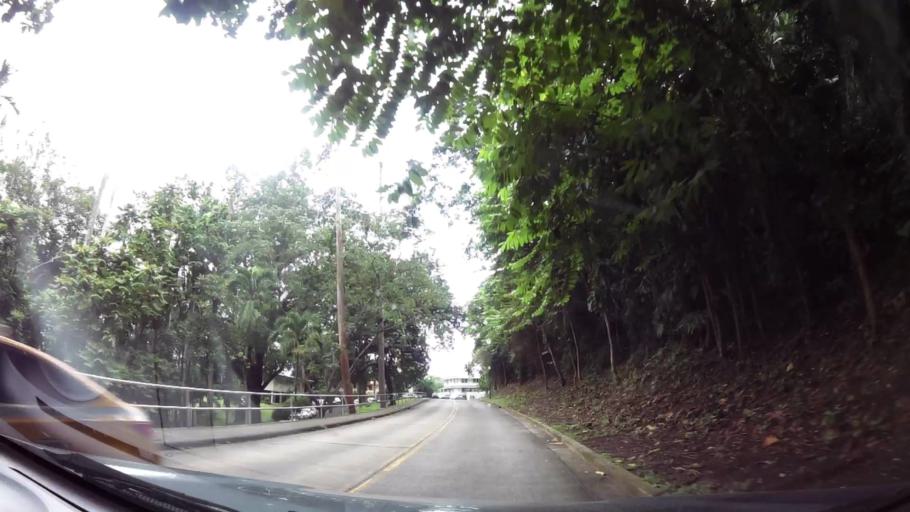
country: PA
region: Panama
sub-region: Distrito de Panama
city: Ancon
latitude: 8.9615
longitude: -79.5508
